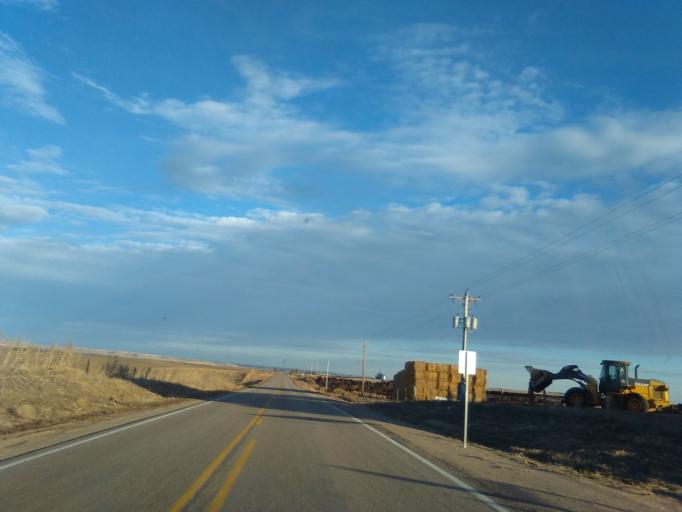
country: US
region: Nebraska
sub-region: Morrill County
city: Bridgeport
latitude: 41.5981
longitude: -102.9740
